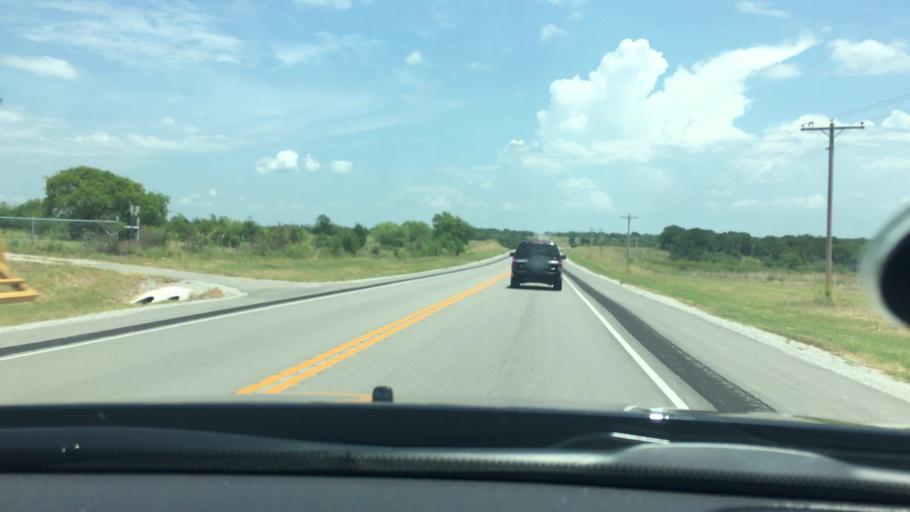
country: US
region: Oklahoma
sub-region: Love County
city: Marietta
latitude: 33.9404
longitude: -97.2205
